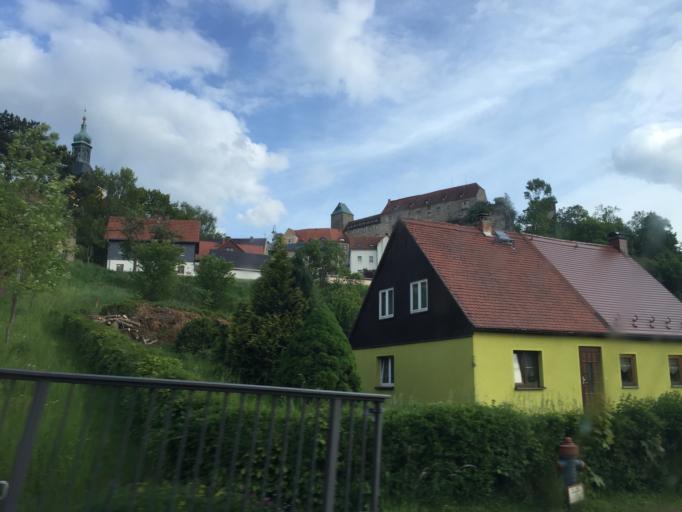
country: DE
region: Saxony
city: Hohnstein
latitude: 50.9815
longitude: 14.1079
